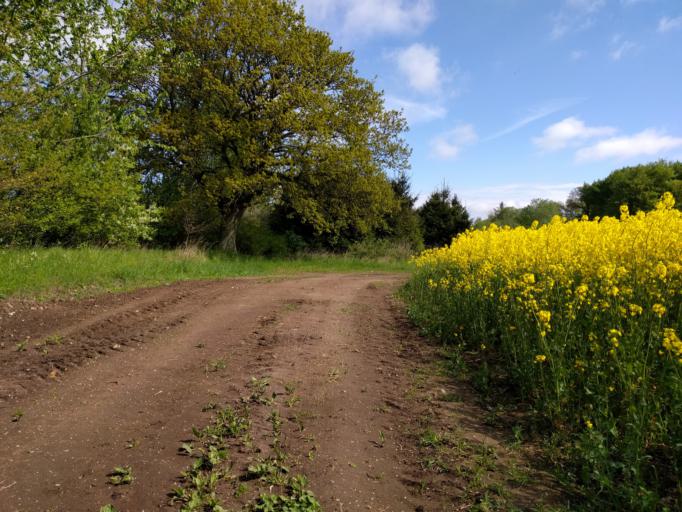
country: DK
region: South Denmark
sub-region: Kerteminde Kommune
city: Langeskov
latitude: 55.3859
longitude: 10.5573
